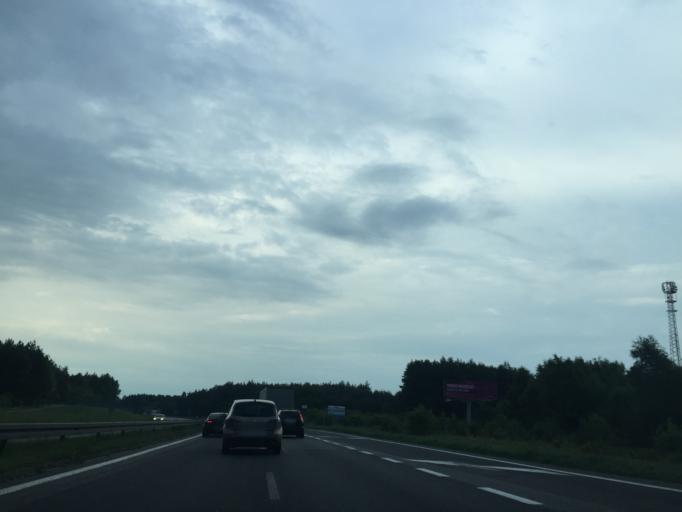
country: PL
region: Masovian Voivodeship
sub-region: Powiat ostrowski
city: Ostrow Mazowiecka
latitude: 52.7876
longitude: 21.8639
